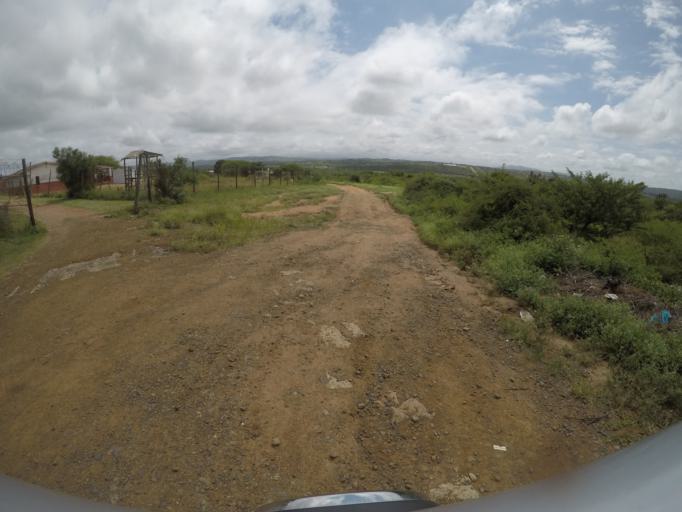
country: ZA
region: KwaZulu-Natal
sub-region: uThungulu District Municipality
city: Empangeni
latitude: -28.5759
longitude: 31.8437
